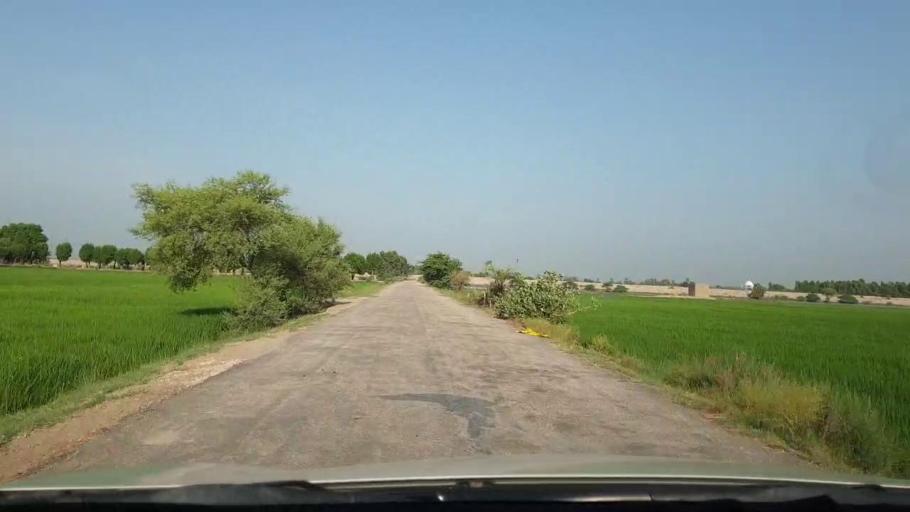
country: PK
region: Sindh
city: Larkana
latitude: 27.5455
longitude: 68.2598
